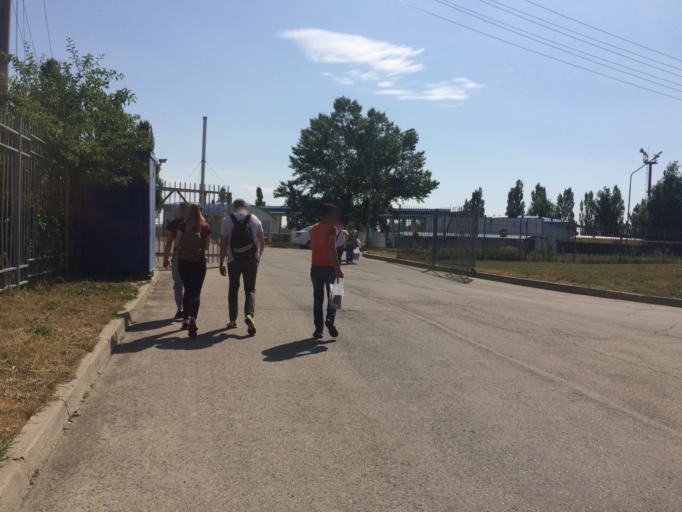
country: RU
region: Stavropol'skiy
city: Tatarka
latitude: 44.9904
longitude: 41.9357
